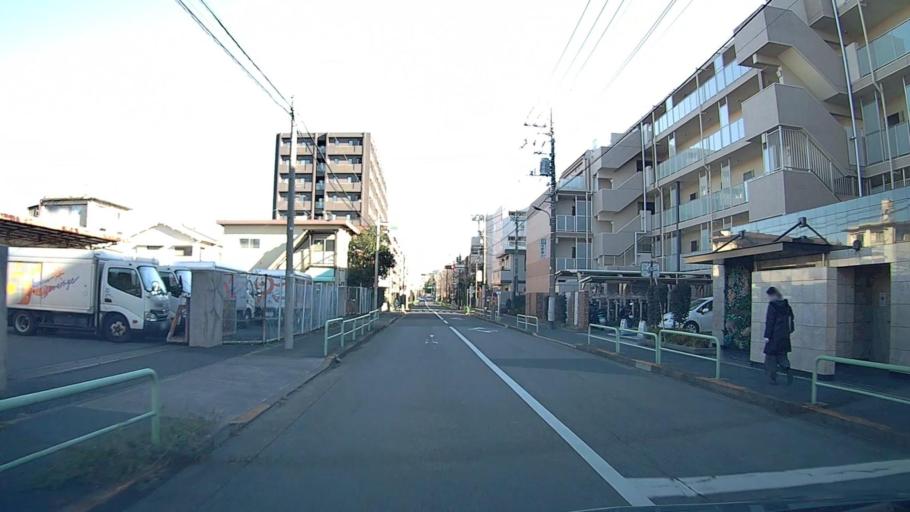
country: JP
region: Tokyo
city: Tokyo
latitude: 35.7289
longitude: 139.6435
